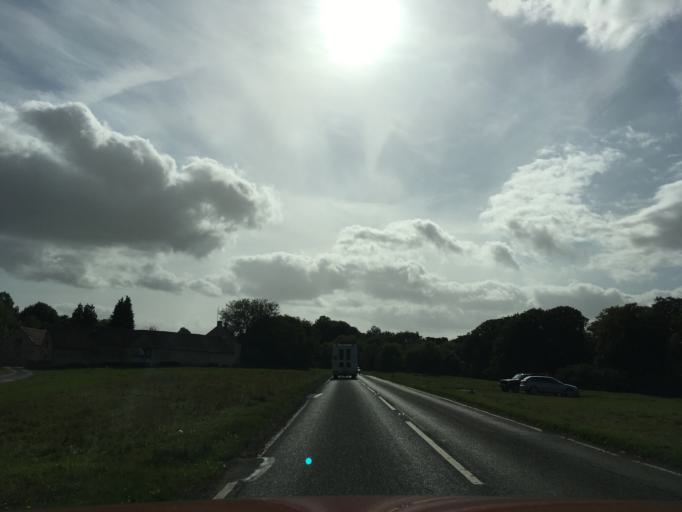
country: GB
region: England
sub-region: Gloucestershire
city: Nailsworth
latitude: 51.7212
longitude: -2.2523
